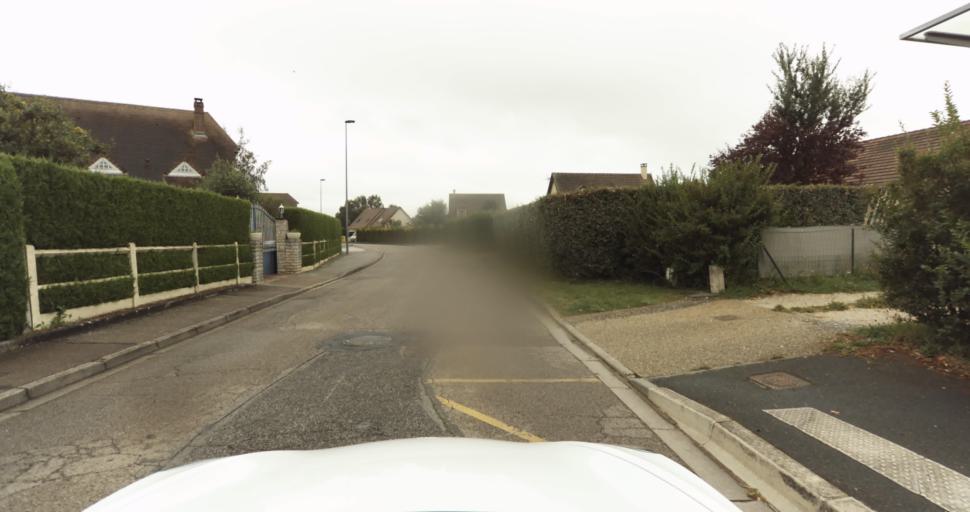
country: FR
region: Haute-Normandie
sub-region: Departement de l'Eure
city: Aviron
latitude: 49.0428
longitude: 1.1374
